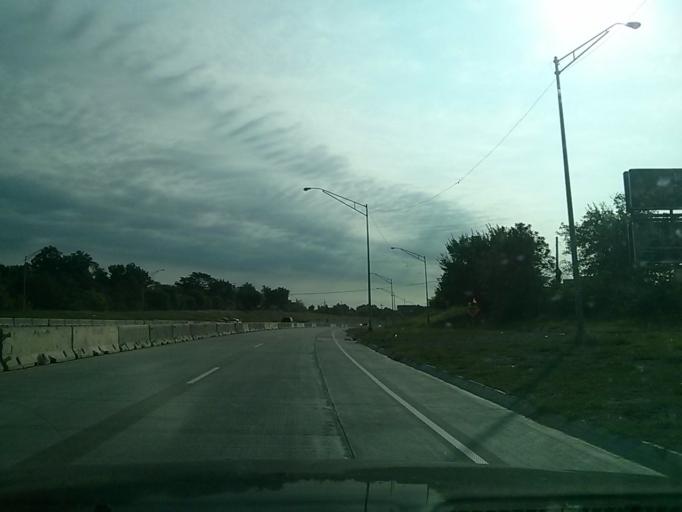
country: US
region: Oklahoma
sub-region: Tulsa County
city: Tulsa
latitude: 36.1600
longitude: -95.9635
